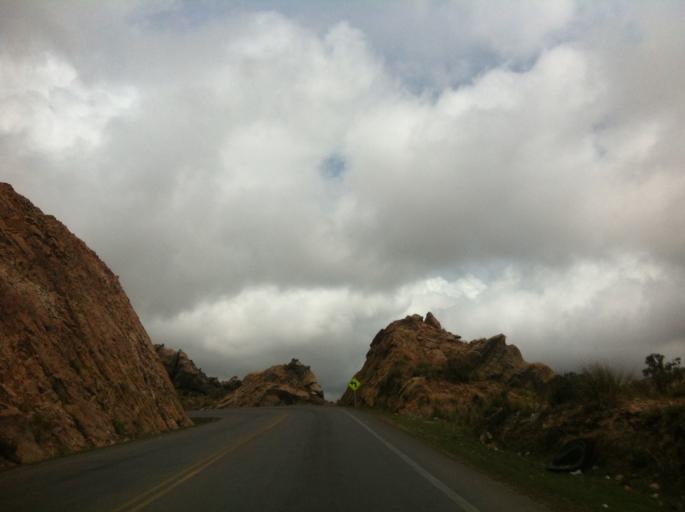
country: BO
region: Cochabamba
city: Irpa Irpa
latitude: -17.7020
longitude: -66.4799
